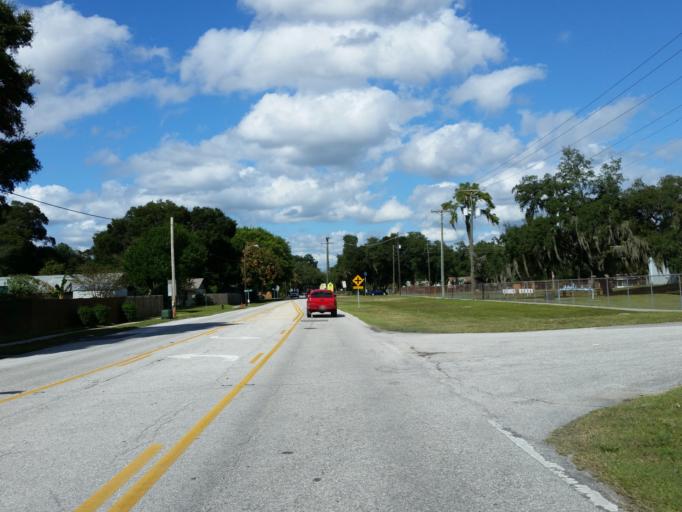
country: US
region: Florida
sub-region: Hillsborough County
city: Brandon
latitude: 27.9067
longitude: -82.2774
